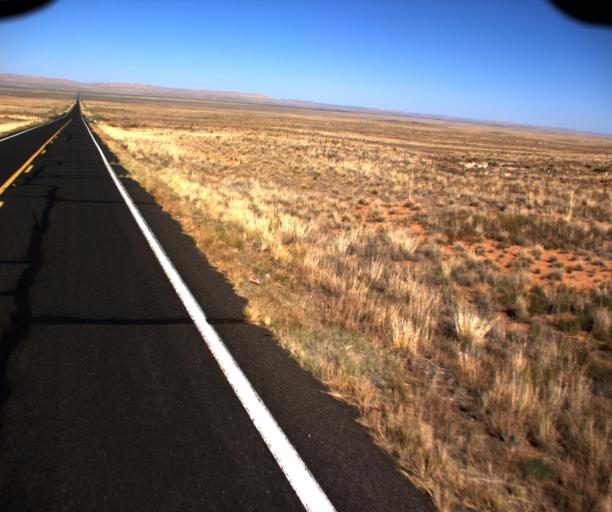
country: US
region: Arizona
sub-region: Navajo County
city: First Mesa
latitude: 35.6431
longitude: -110.4865
